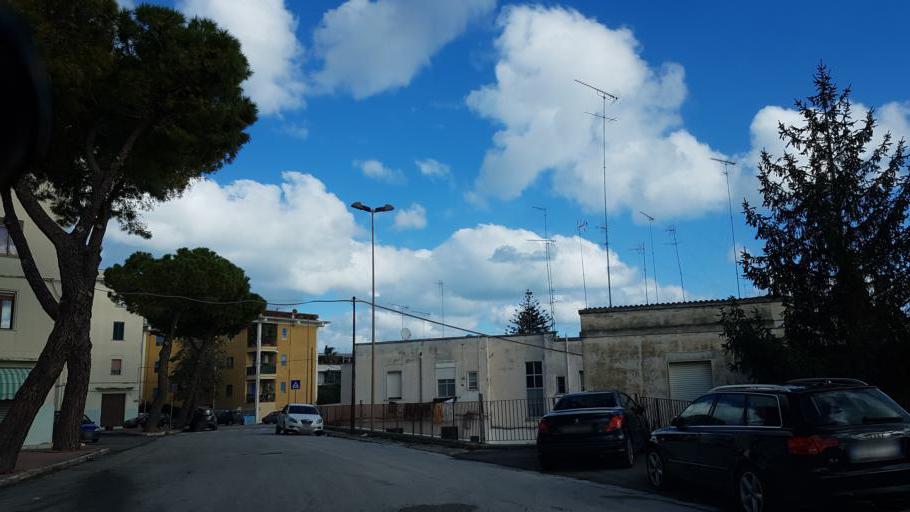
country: IT
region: Apulia
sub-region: Provincia di Brindisi
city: Brindisi
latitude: 40.6440
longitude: 17.9404
